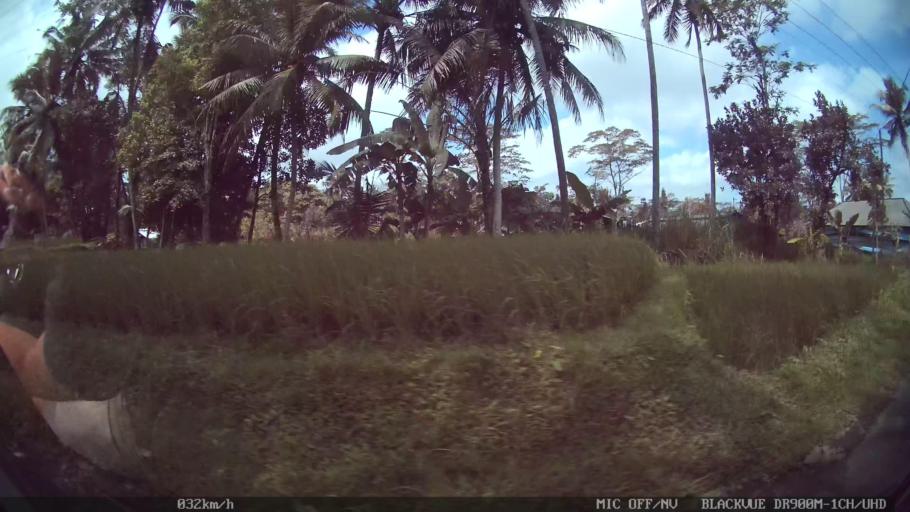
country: ID
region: Bali
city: Banjar Abuan
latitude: -8.4623
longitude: 115.3407
